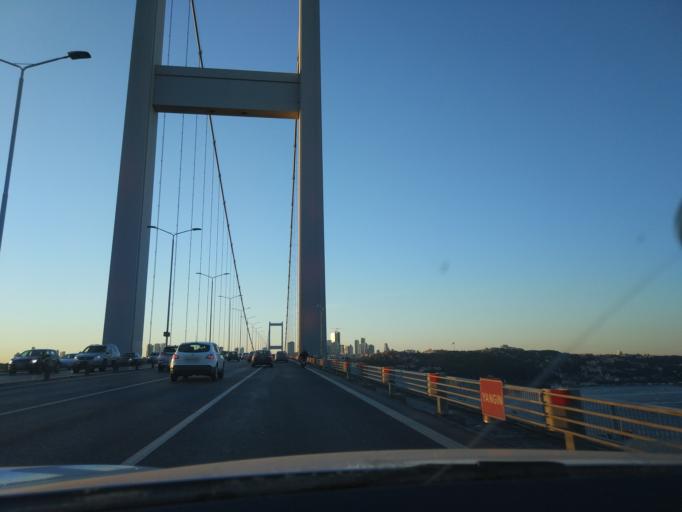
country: TR
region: Istanbul
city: UEskuedar
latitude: 41.0412
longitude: 29.0389
